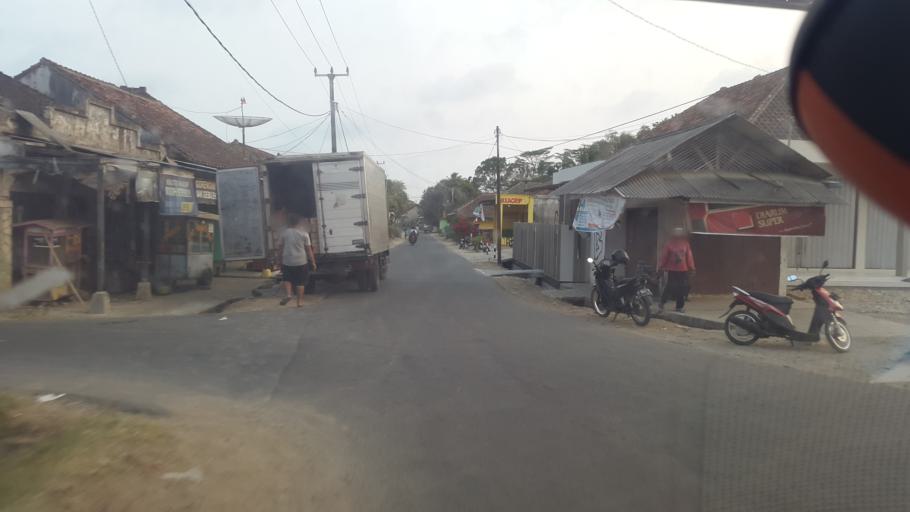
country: ID
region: West Java
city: Cibungur
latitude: -7.3710
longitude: 106.5386
